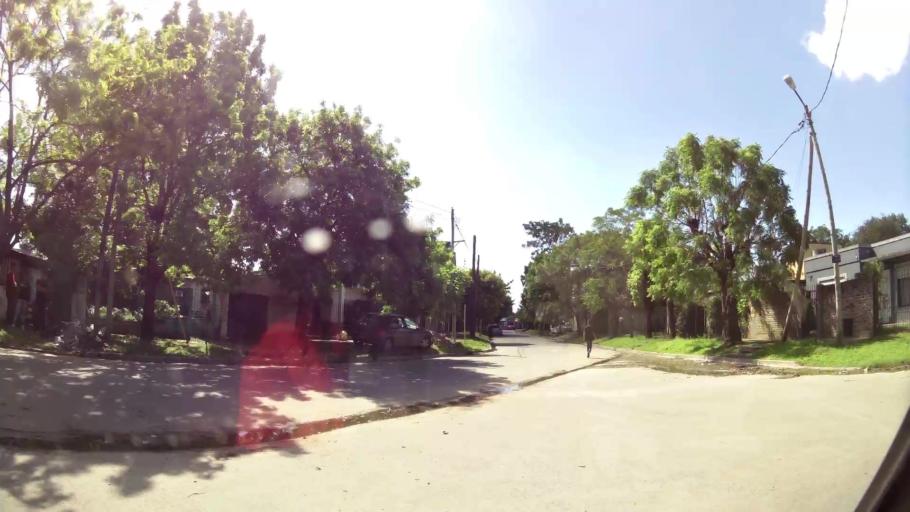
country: AR
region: Buenos Aires
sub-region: Partido de Quilmes
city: Quilmes
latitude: -34.8038
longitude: -58.2659
